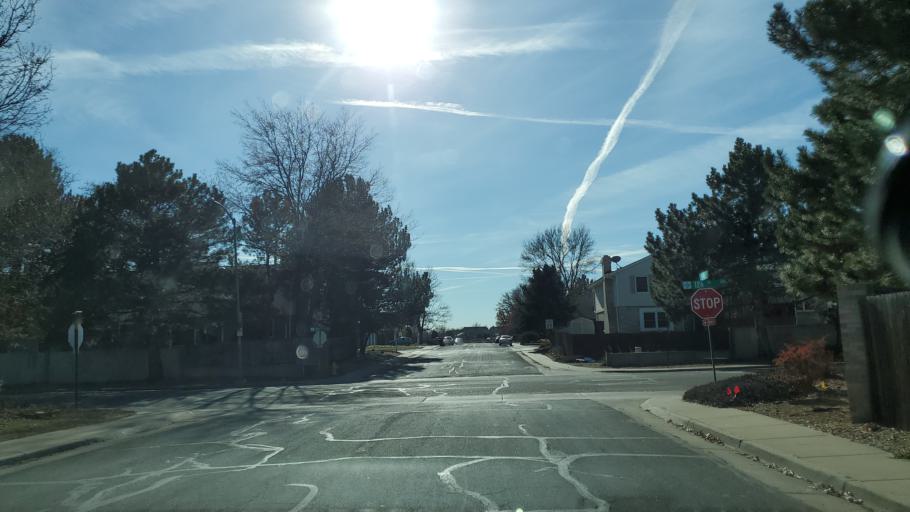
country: US
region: Colorado
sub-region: Adams County
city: Northglenn
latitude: 39.9214
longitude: -104.9521
